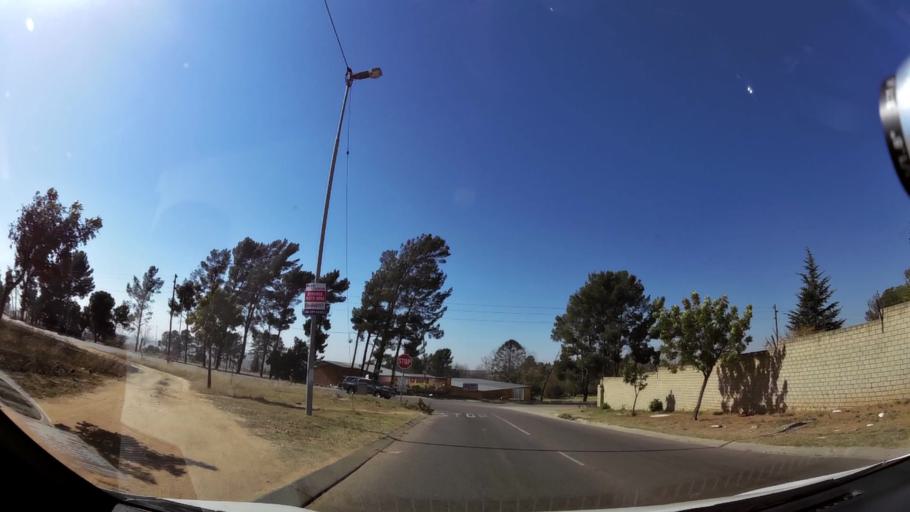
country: ZA
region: Gauteng
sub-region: City of Johannesburg Metropolitan Municipality
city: Midrand
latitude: -25.9420
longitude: 28.0997
